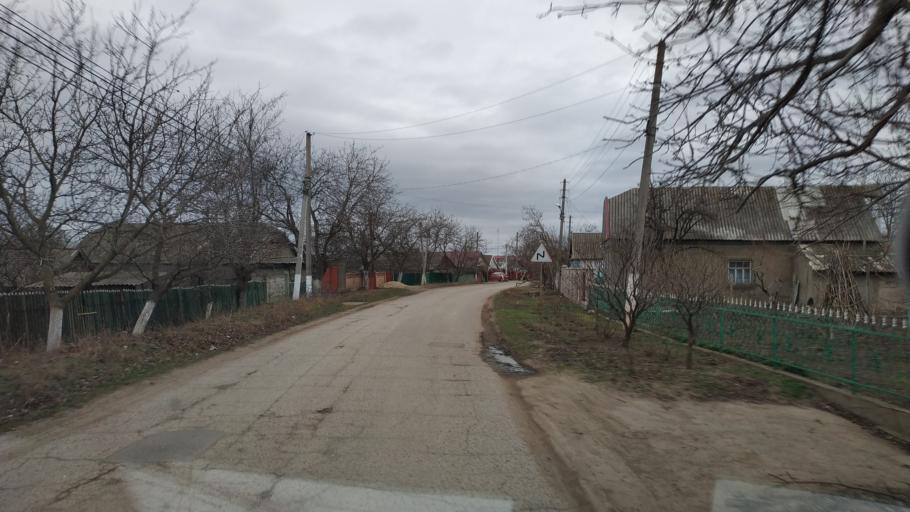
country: MD
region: Bender
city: Bender
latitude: 46.7757
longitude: 29.4835
